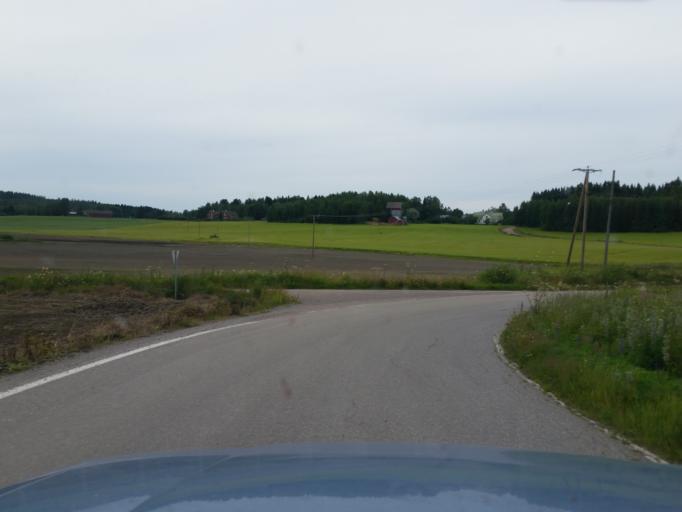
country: FI
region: Uusimaa
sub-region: Helsinki
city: Sammatti
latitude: 60.4740
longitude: 23.8219
